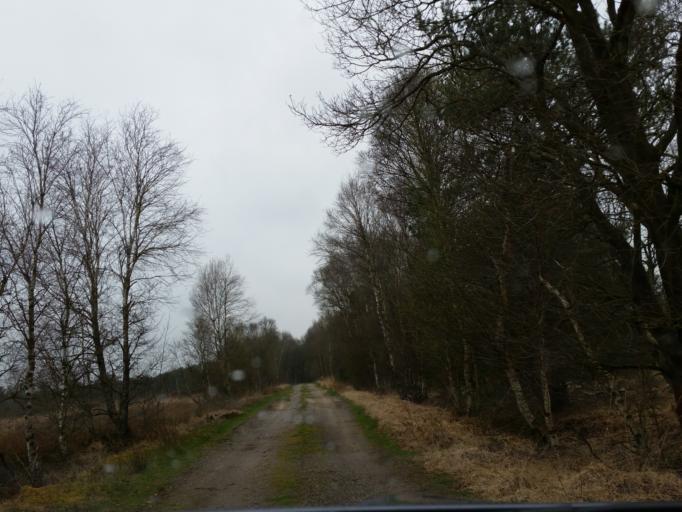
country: DE
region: Lower Saxony
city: Mittelstenahe
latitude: 53.6017
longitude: 8.9973
